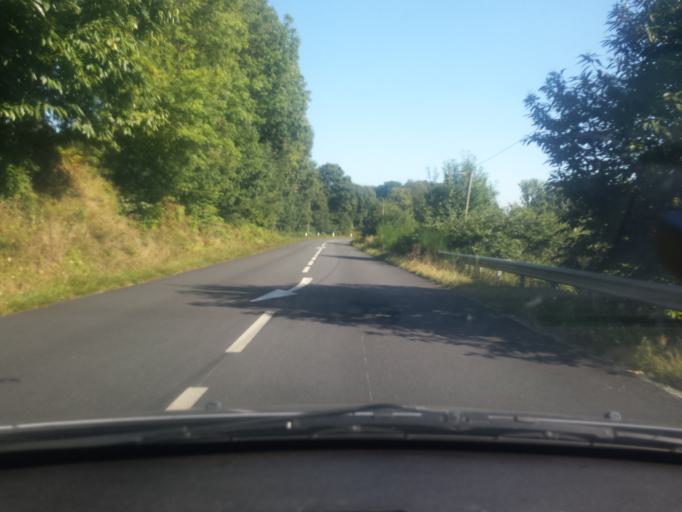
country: FR
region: Brittany
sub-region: Departement du Morbihan
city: Malguenac
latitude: 48.0933
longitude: -3.0186
